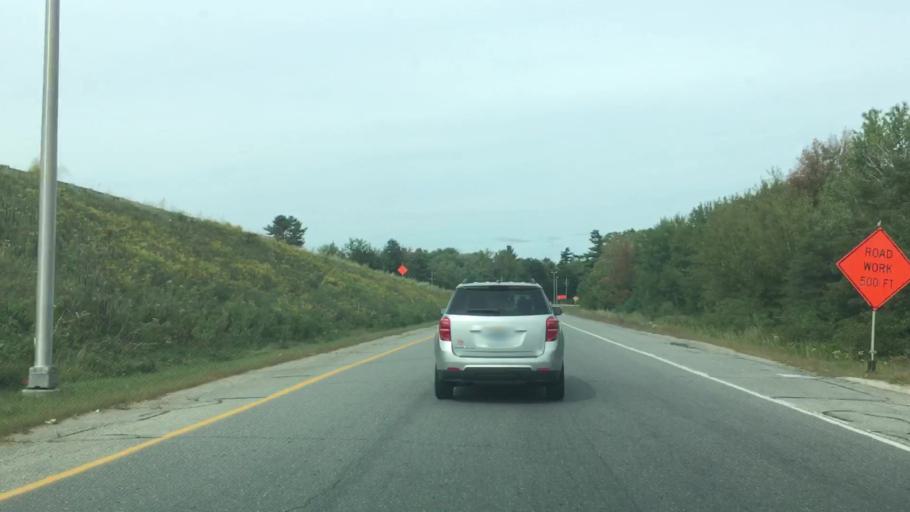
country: US
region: Maine
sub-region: Waldo County
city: Belfast
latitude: 44.4240
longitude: -69.0212
